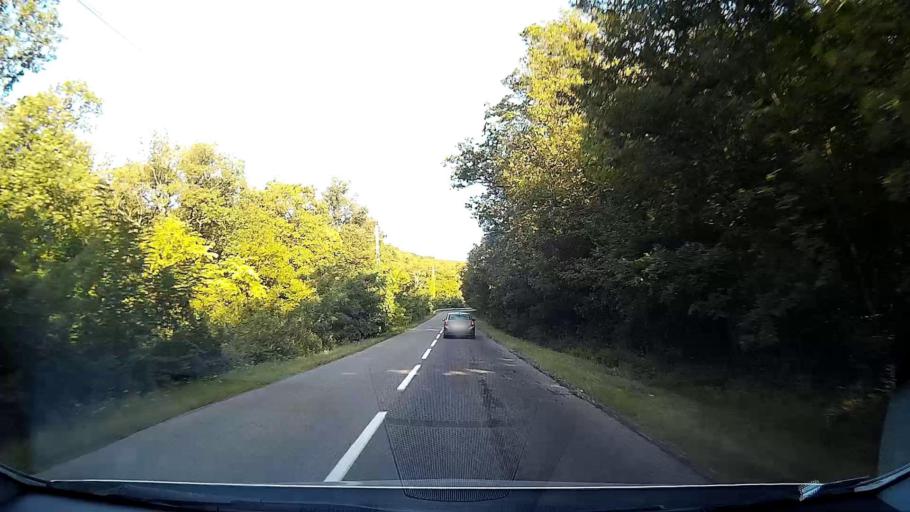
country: HU
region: Pest
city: Nagykovacsi
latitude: 47.7045
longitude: 19.0193
